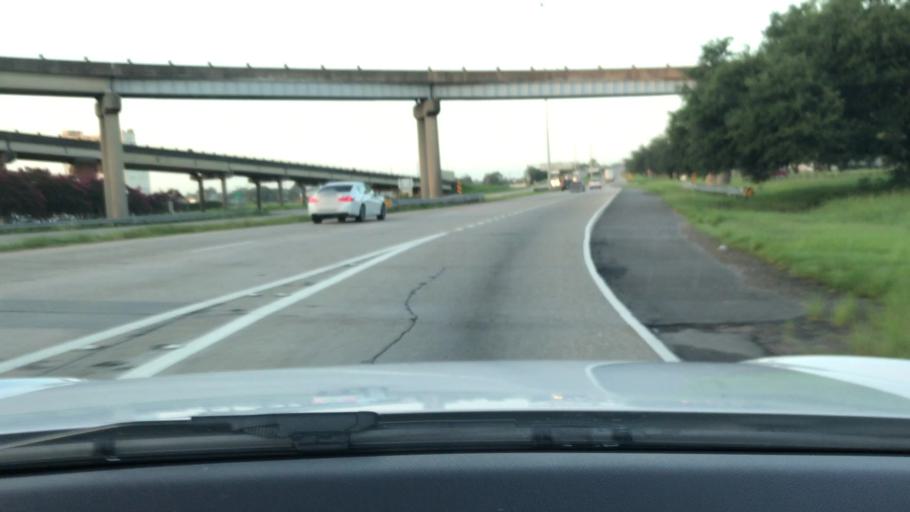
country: US
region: Louisiana
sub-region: West Baton Rouge Parish
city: Port Allen
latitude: 30.4390
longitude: -91.2087
